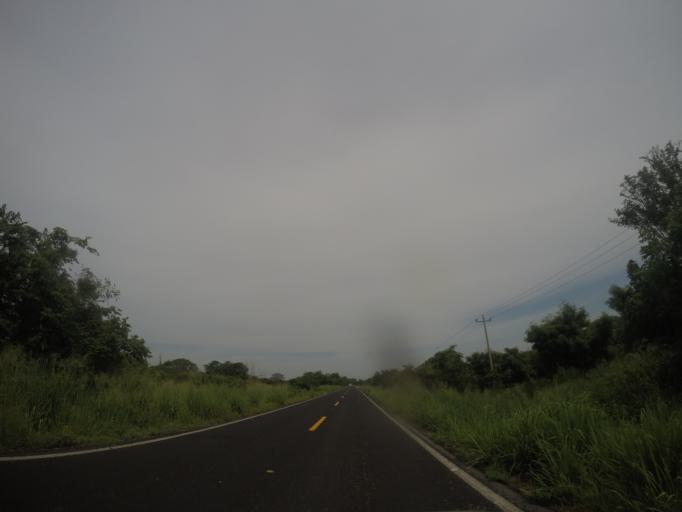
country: MX
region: Oaxaca
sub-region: Villa de Tututepec de Melchor Ocampo
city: Santa Rosa de Lima
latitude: 16.0262
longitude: -97.5617
